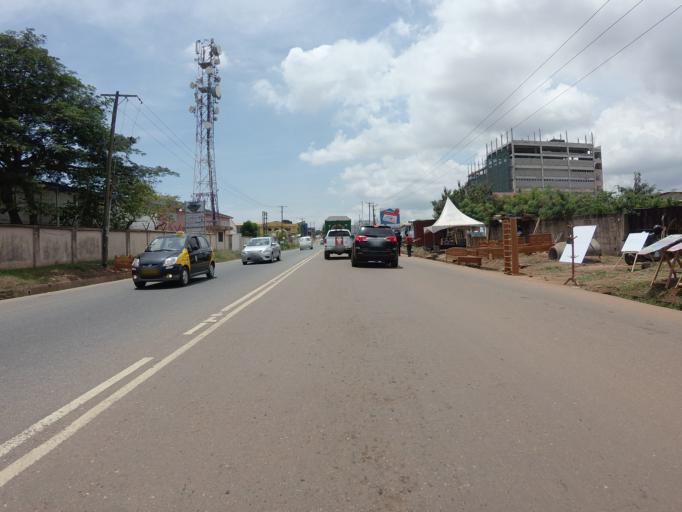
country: GH
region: Greater Accra
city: Medina Estates
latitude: 5.6367
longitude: -0.1288
